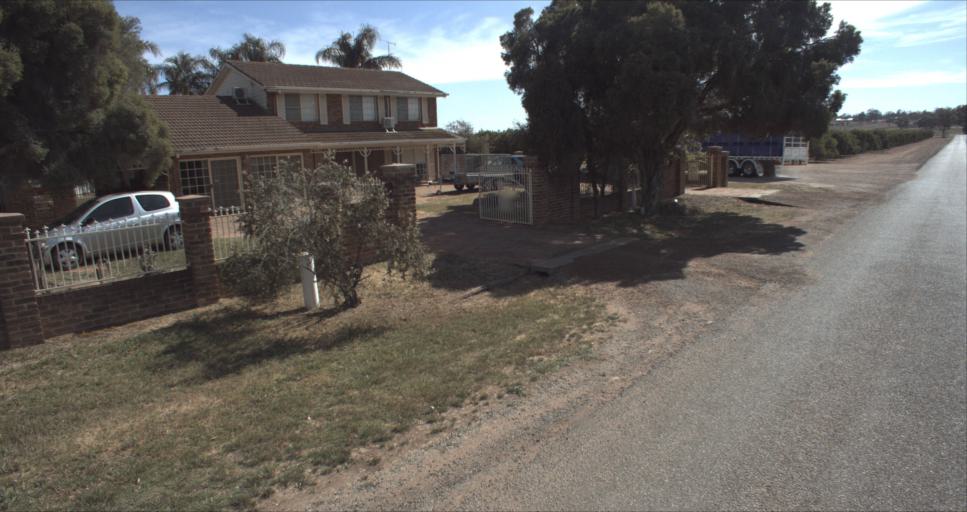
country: AU
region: New South Wales
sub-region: Leeton
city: Leeton
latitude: -34.5879
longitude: 146.4736
